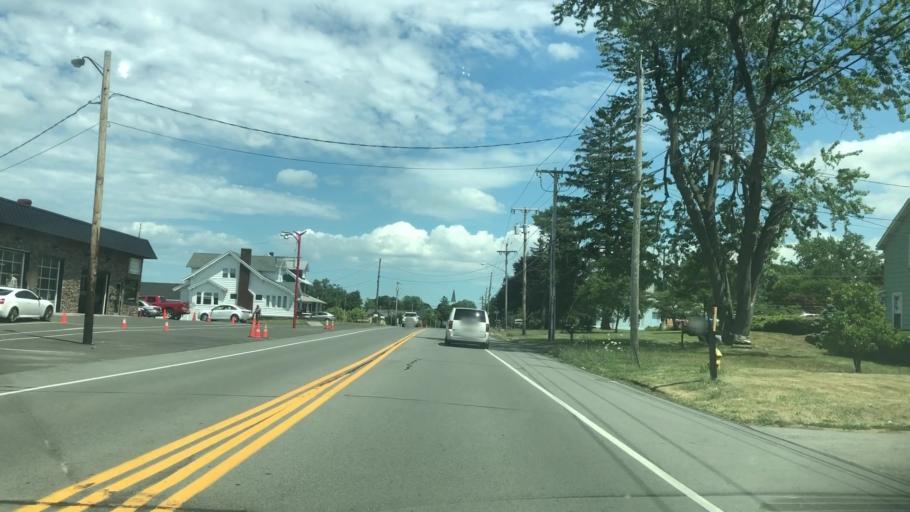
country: US
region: New York
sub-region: Monroe County
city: Webster
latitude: 43.2107
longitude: -77.4412
